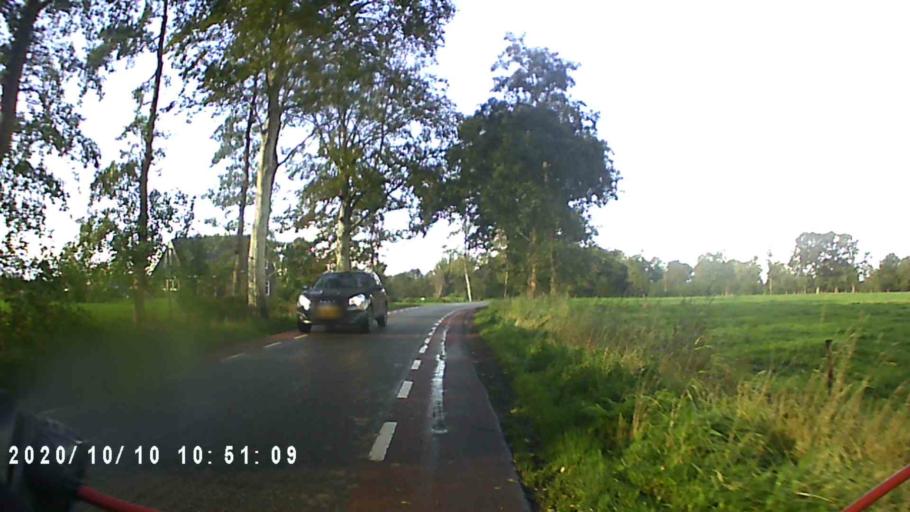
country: NL
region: Friesland
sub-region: Gemeente Achtkarspelen
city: Surhuisterveen
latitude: 53.1594
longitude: 6.2306
